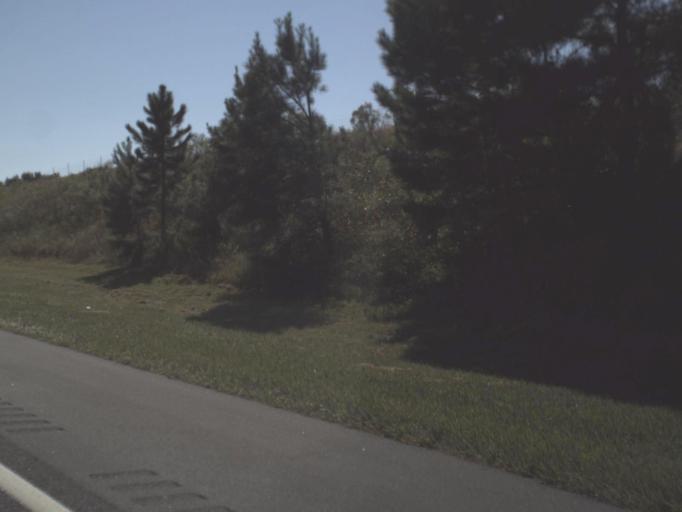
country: US
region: Florida
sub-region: Lake County
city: Hawthorne
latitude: 28.7040
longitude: -81.8848
